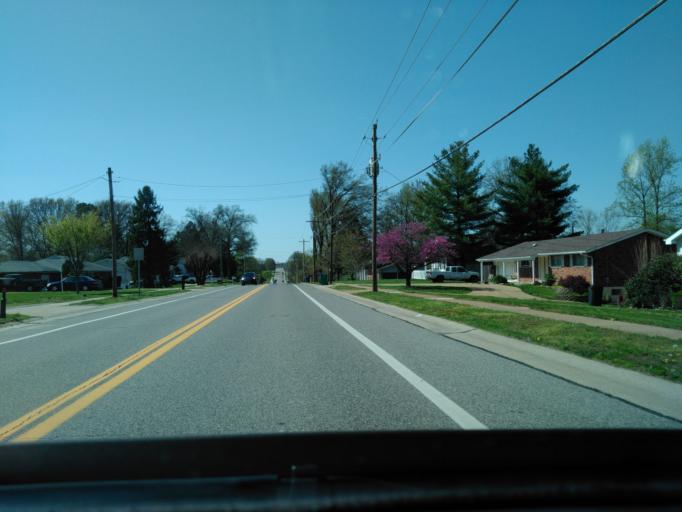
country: US
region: Missouri
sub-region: Saint Louis County
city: Concord
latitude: 38.5023
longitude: -90.3635
